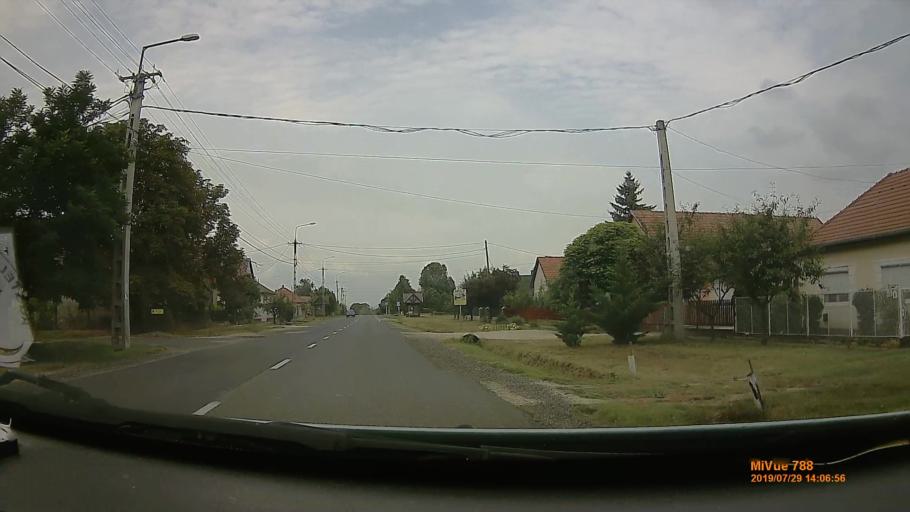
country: HU
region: Somogy
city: Balatonfoldvar
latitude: 46.8209
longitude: 17.9059
